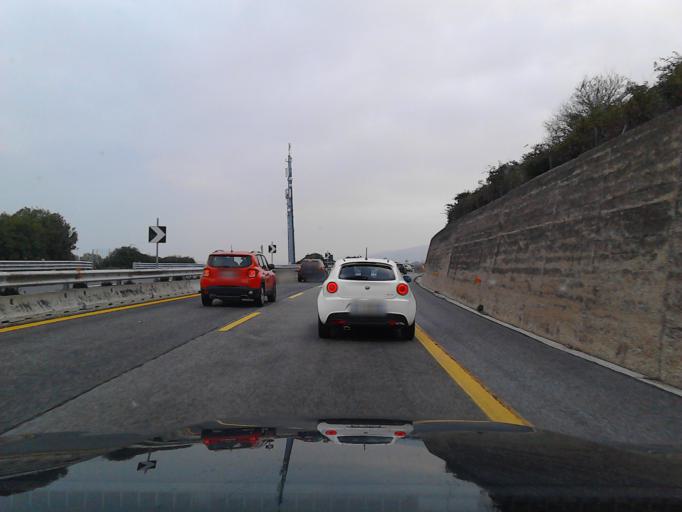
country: IT
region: Abruzzo
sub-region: Provincia di Teramo
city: Tortoreto Lido
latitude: 42.7943
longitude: 13.9334
